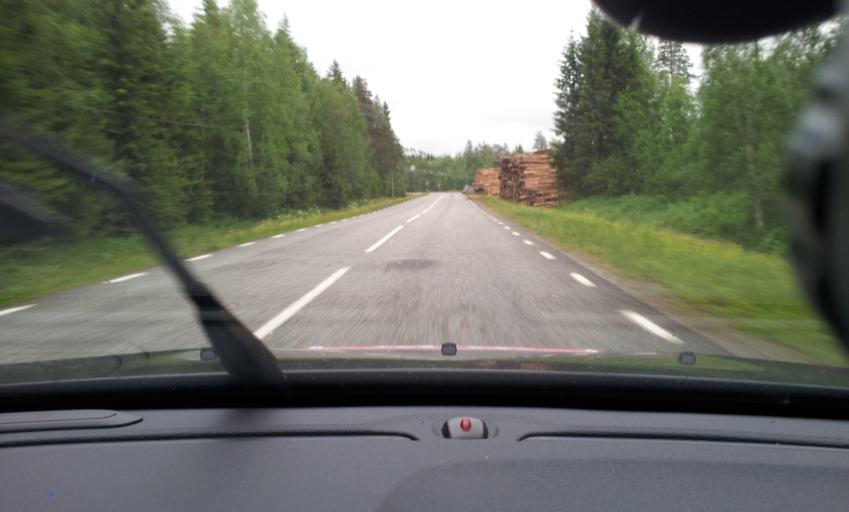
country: SE
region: Jaemtland
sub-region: Stroemsunds Kommun
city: Stroemsund
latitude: 63.3428
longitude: 15.7553
